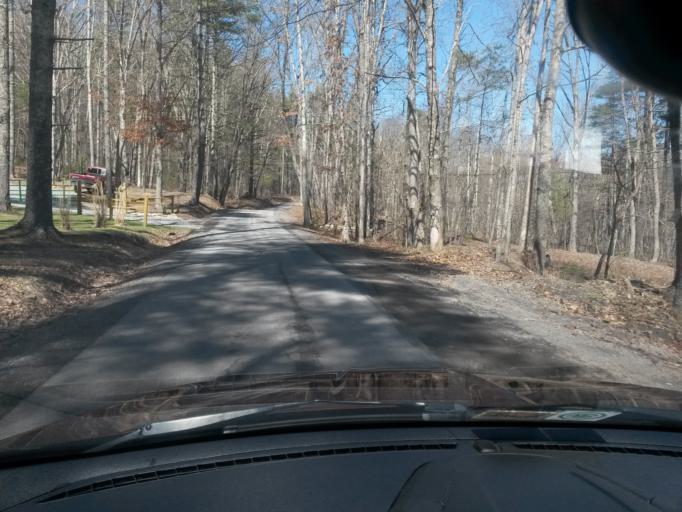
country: US
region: West Virginia
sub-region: Greenbrier County
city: White Sulphur Springs
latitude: 37.6397
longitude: -80.3354
